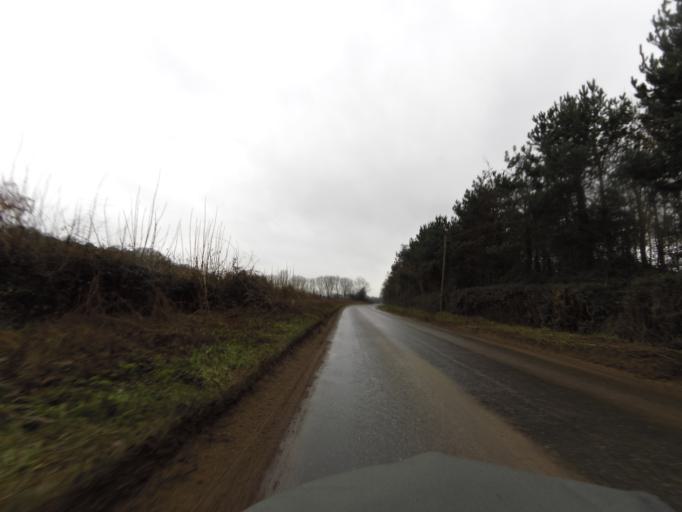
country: GB
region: England
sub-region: Norfolk
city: Briston
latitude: 52.8923
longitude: 1.0862
